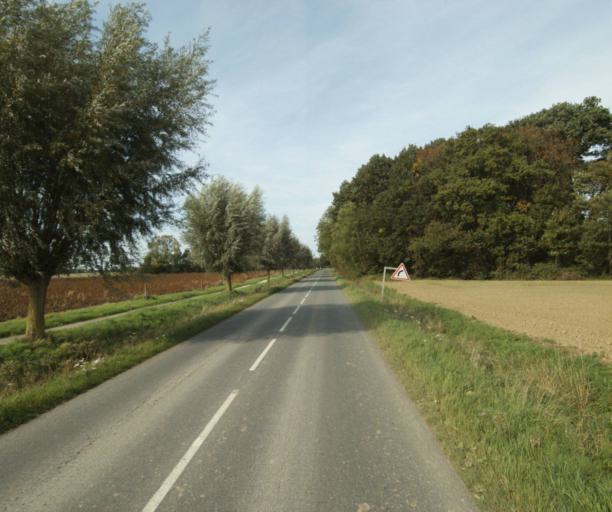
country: FR
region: Nord-Pas-de-Calais
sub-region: Departement du Nord
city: Radinghem-en-Weppes
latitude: 50.6106
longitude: 2.9097
